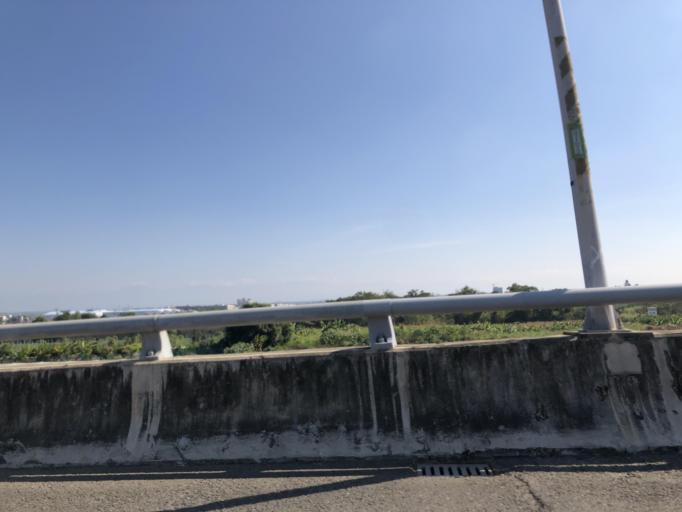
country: TW
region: Taiwan
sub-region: Tainan
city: Tainan
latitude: 23.0182
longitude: 120.2890
